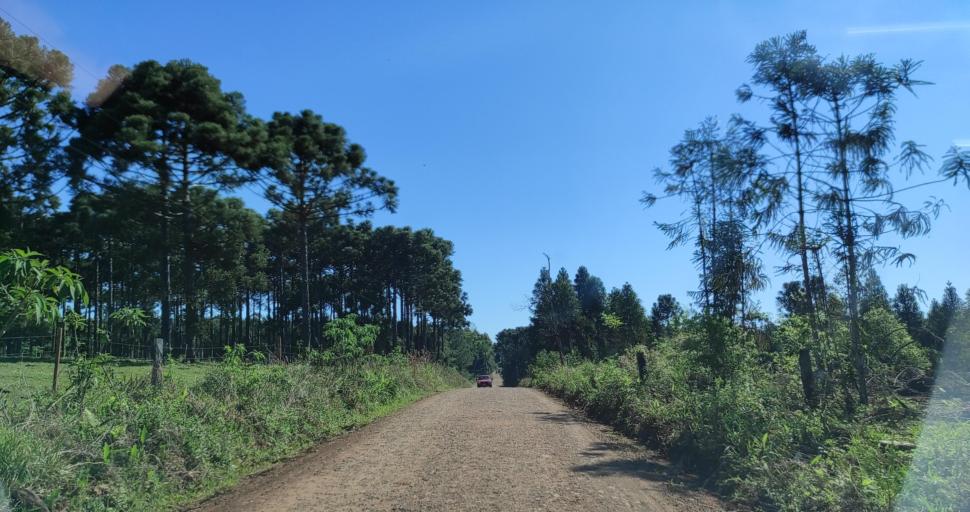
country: AR
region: Misiones
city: Capiovi
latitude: -26.9346
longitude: -55.0035
